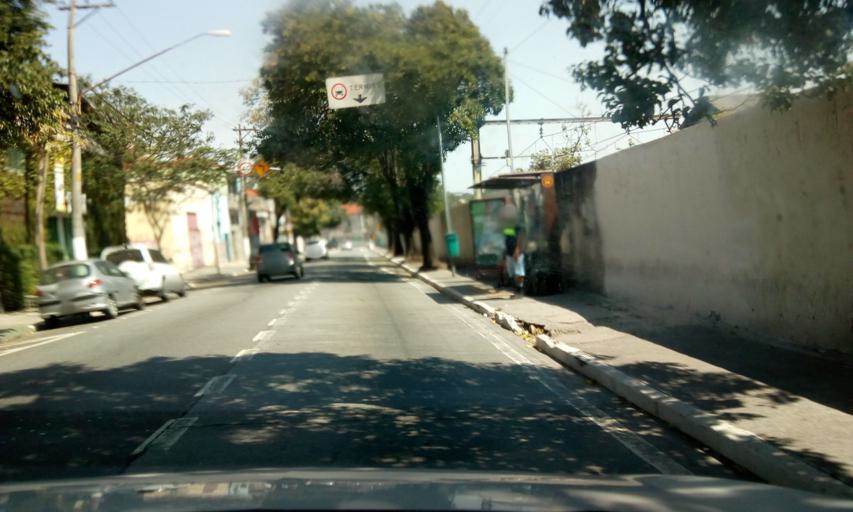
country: BR
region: Sao Paulo
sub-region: Sao Paulo
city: Sao Paulo
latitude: -23.5184
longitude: -46.7085
